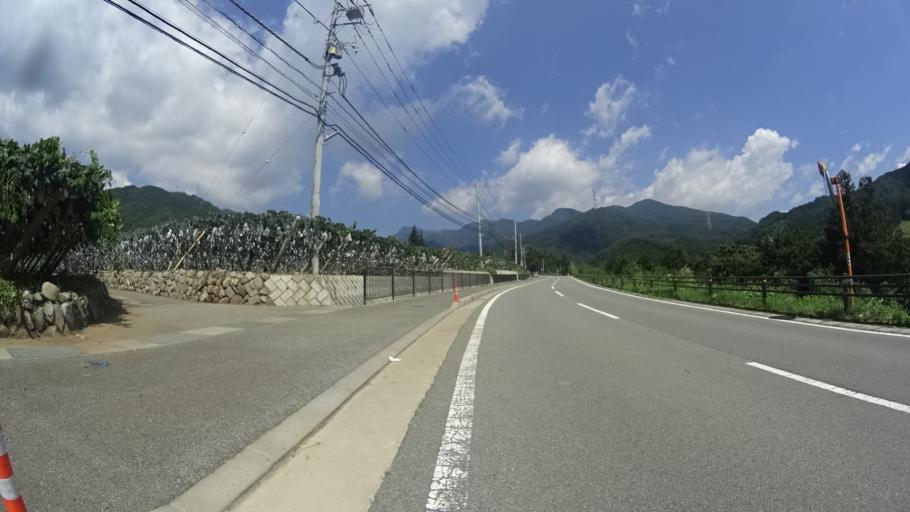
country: JP
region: Yamanashi
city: Enzan
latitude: 35.7591
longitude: 138.7064
